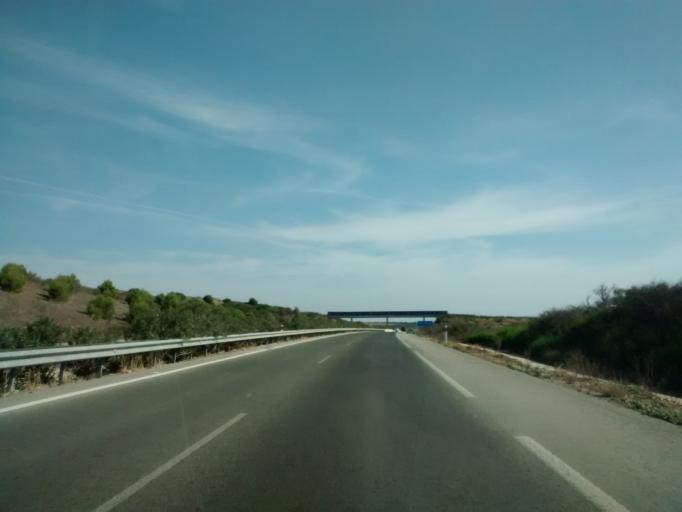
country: ES
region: Andalusia
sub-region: Provincia de Cadiz
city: Conil de la Frontera
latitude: 36.3254
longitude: -6.0554
